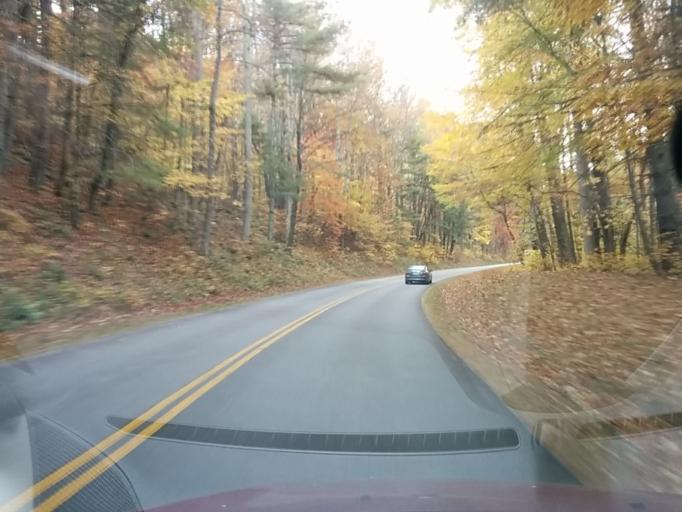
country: US
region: Virginia
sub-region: City of Buena Vista
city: Buena Vista
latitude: 37.8063
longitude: -79.2216
